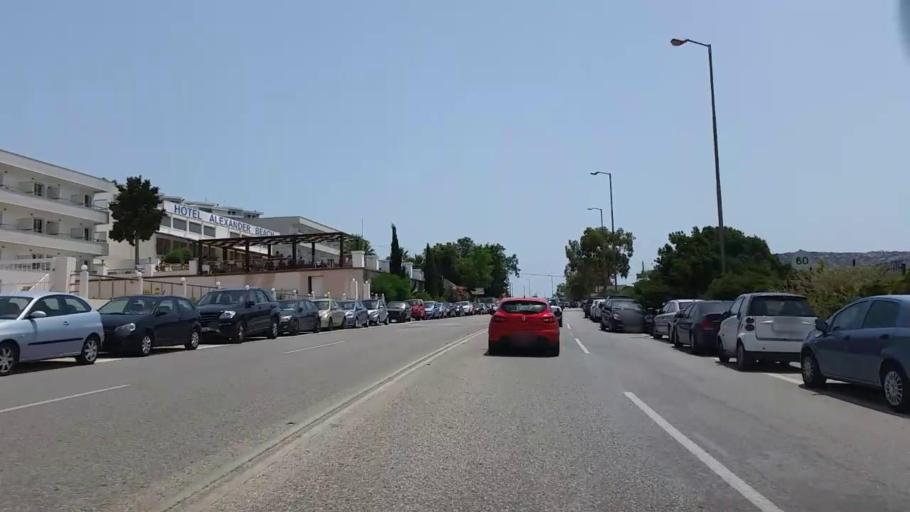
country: GR
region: Attica
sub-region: Nomarchia Anatolikis Attikis
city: Saronida
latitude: 37.7266
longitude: 23.9082
